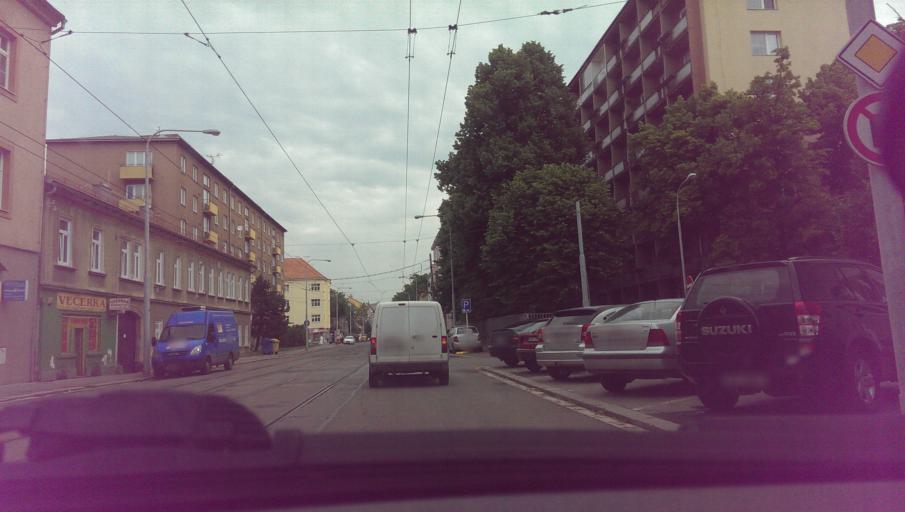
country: CZ
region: South Moravian
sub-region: Mesto Brno
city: Brno
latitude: 49.2052
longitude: 16.6261
